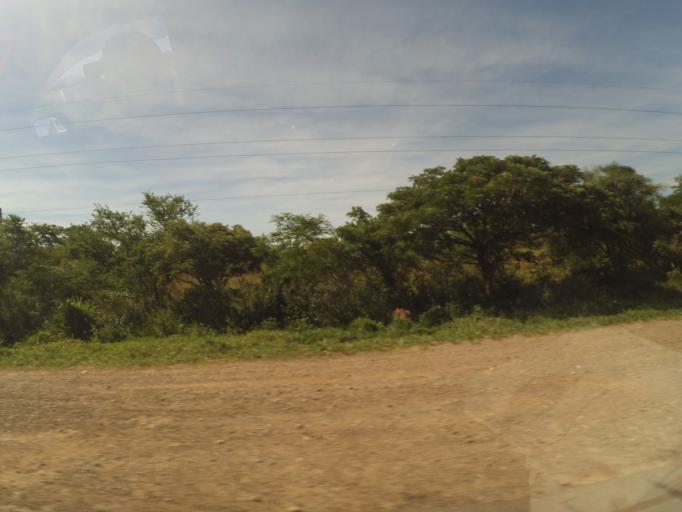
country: BO
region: Santa Cruz
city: San Julian
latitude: -17.7280
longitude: -62.9204
